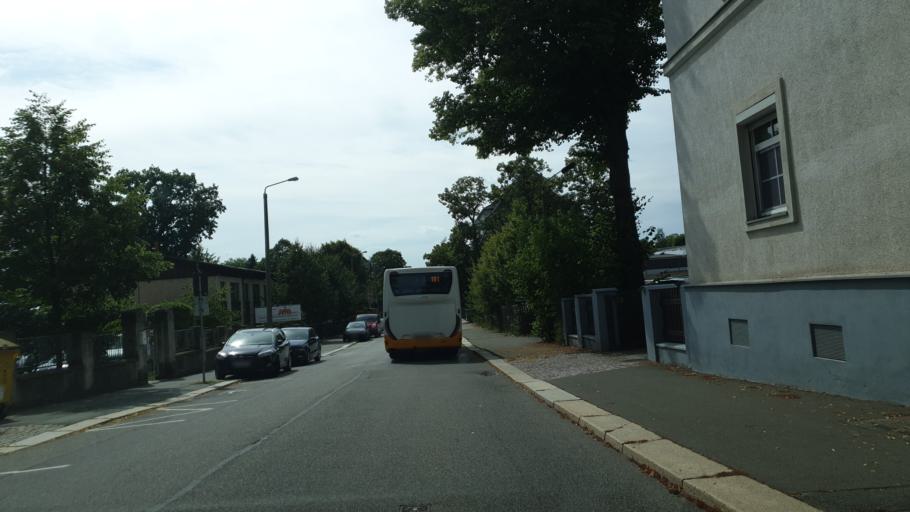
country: DE
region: Saxony
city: Hohenstein-Ernstthal
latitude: 50.7967
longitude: 12.7101
